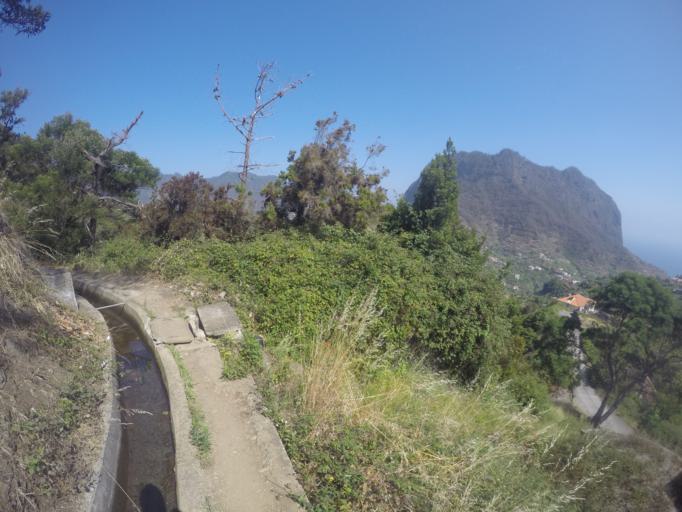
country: PT
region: Madeira
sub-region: Santana
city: Santana
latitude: 32.7558
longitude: -16.8394
